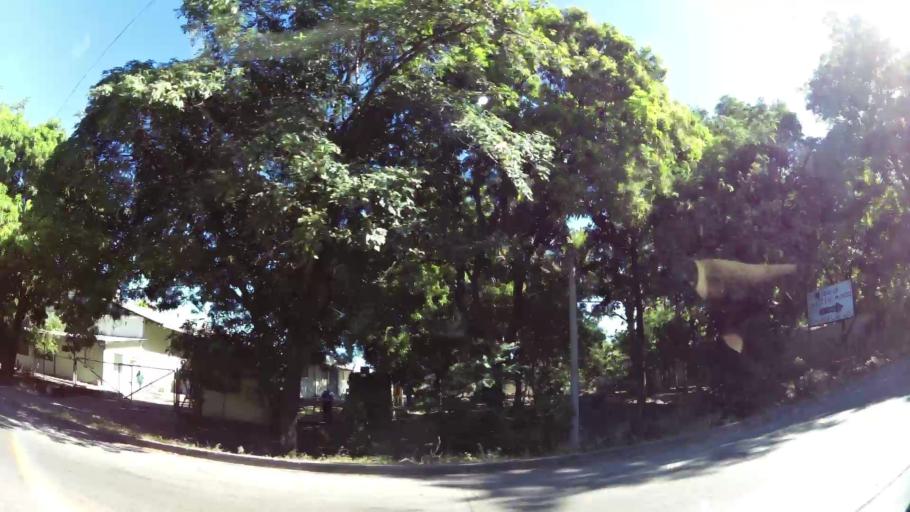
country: SV
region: San Miguel
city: San Miguel
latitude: 13.4564
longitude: -88.1436
